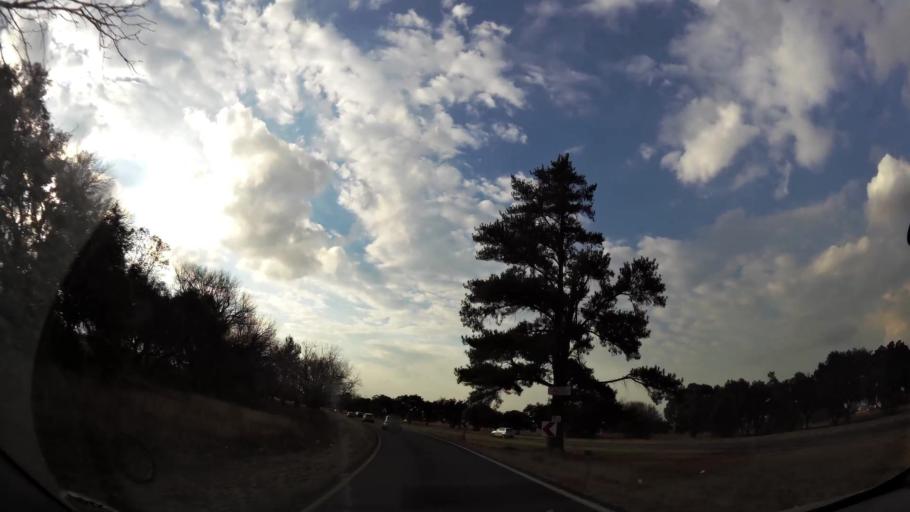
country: ZA
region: Orange Free State
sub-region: Fezile Dabi District Municipality
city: Sasolburg
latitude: -26.8000
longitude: 27.8317
